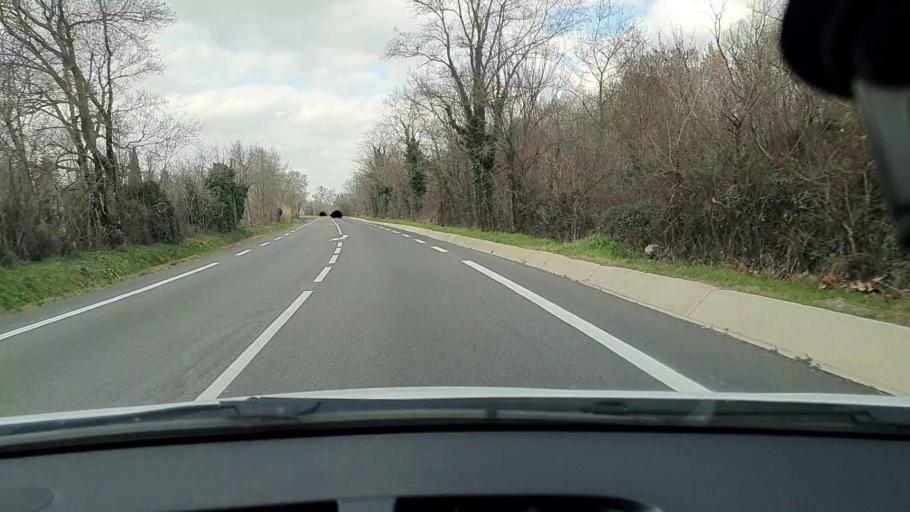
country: FR
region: Languedoc-Roussillon
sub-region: Departement du Gard
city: Vallabregues
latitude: 43.8346
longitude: 4.6204
